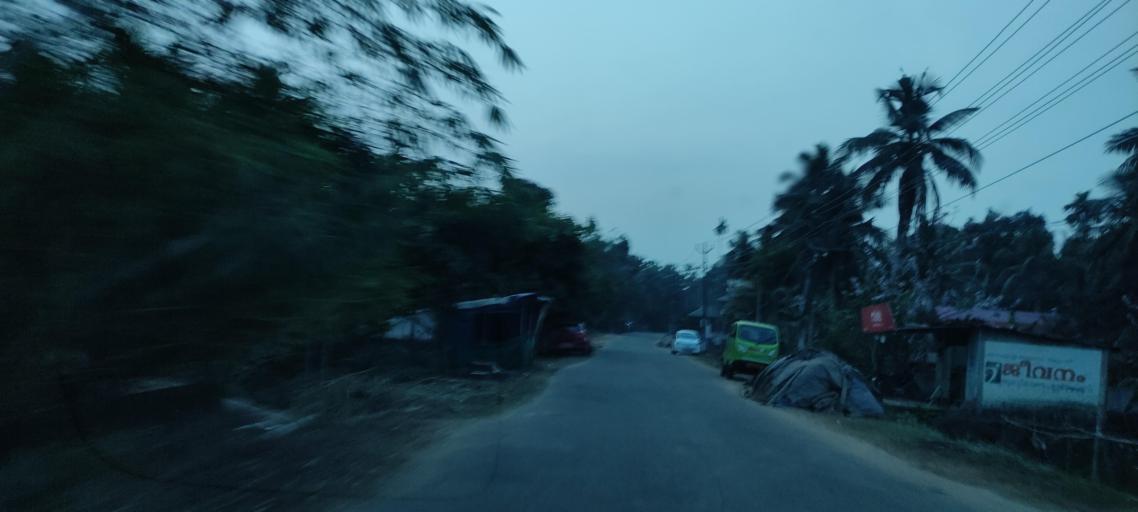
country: IN
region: Kerala
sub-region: Alappuzha
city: Mavelikara
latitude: 9.3297
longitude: 76.4685
